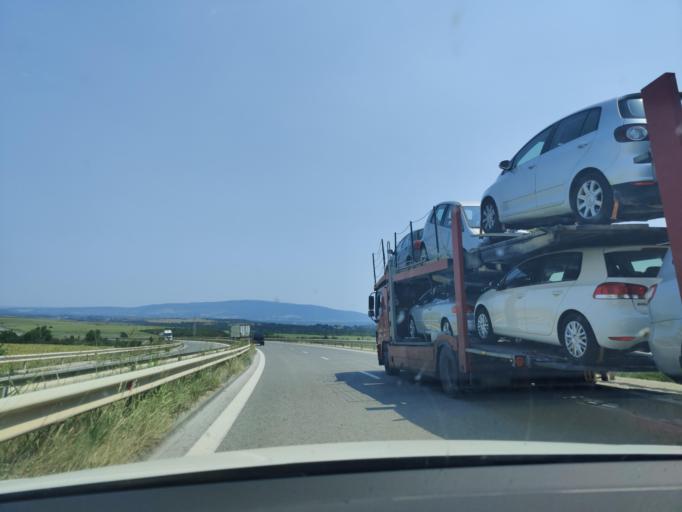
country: BG
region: Montana
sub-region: Obshtina Montana
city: Montana
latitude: 43.4234
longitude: 23.1622
